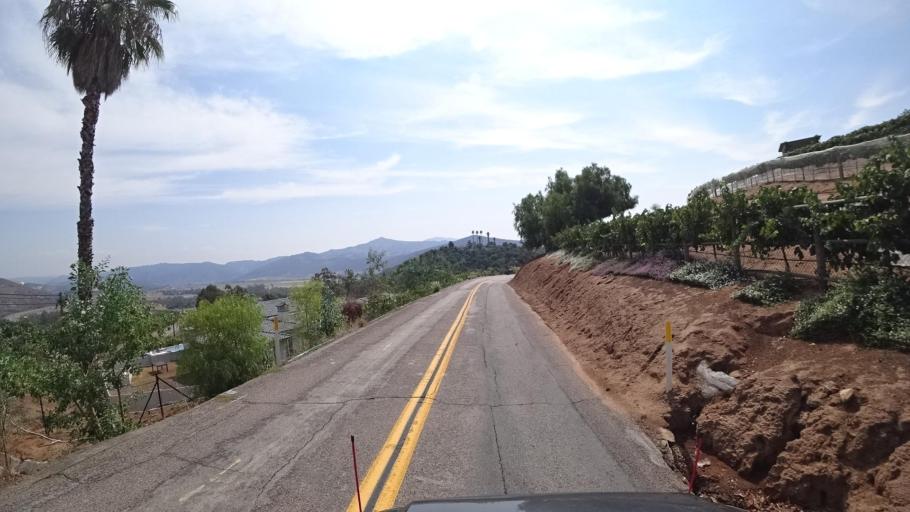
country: US
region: California
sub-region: San Diego County
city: Escondido
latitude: 33.0999
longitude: -117.0313
